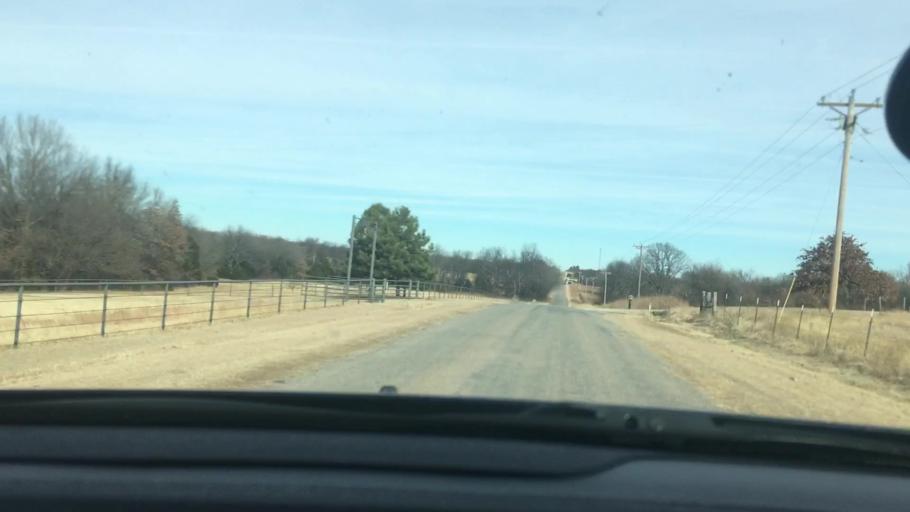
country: US
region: Oklahoma
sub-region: Garvin County
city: Wynnewood
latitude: 34.6384
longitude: -97.2475
